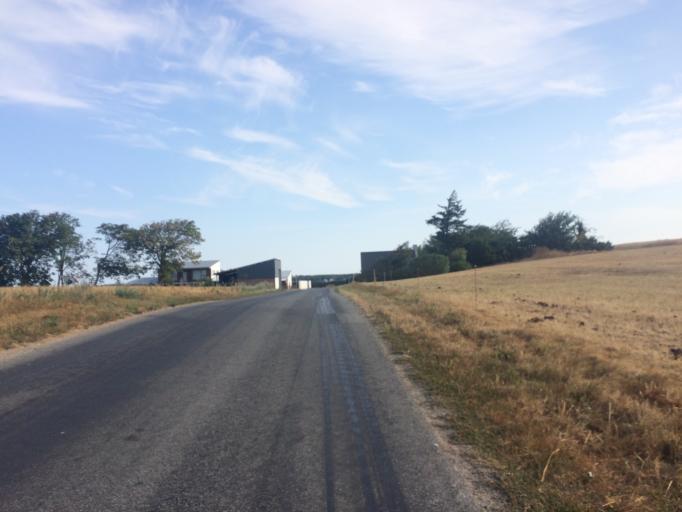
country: DK
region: Central Jutland
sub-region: Holstebro Kommune
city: Vinderup
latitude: 56.5919
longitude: 8.7565
